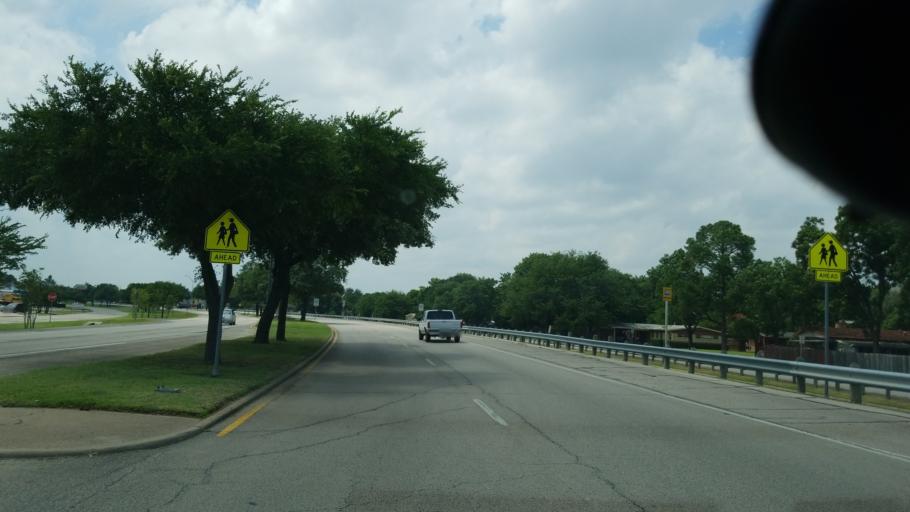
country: US
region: Texas
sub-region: Dallas County
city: Irving
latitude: 32.8245
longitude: -96.9676
